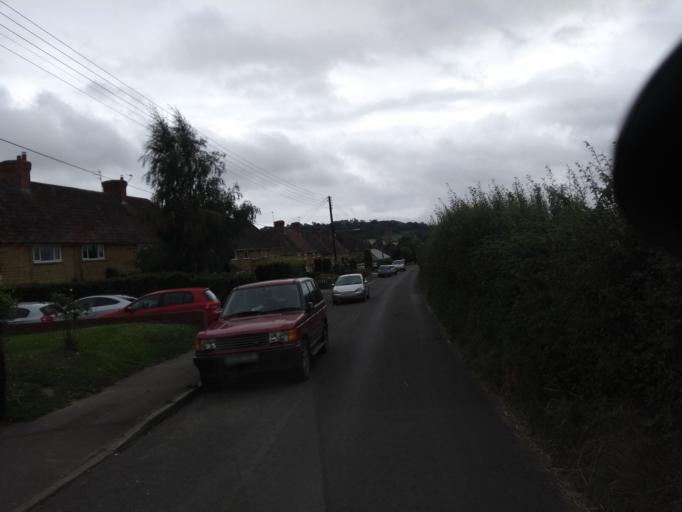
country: GB
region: England
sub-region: Somerset
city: Stoke-sub-Hamdon
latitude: 50.9457
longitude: -2.7557
